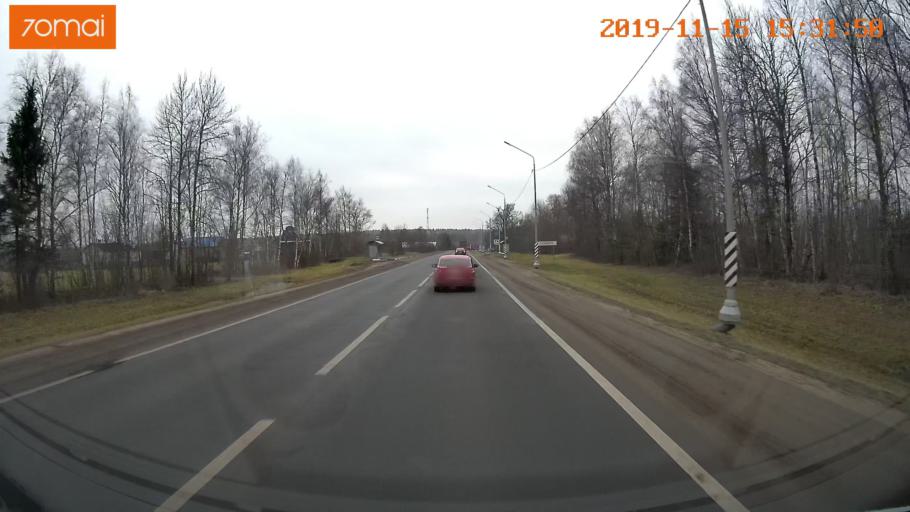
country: RU
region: Jaroslavl
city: Danilov
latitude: 58.0959
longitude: 40.1047
